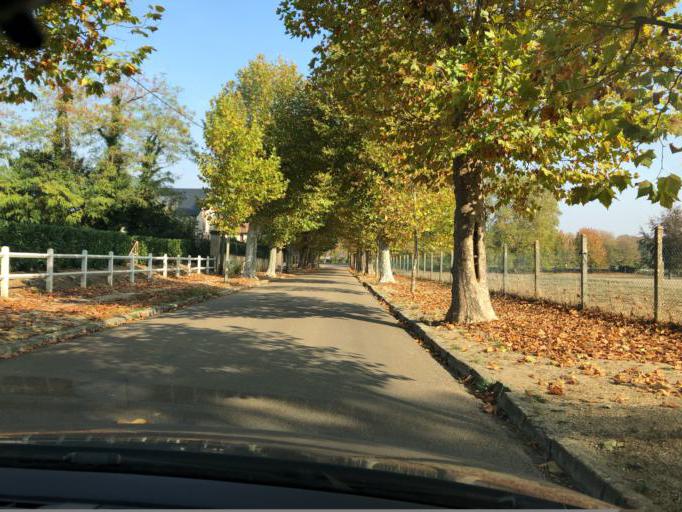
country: FR
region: Bourgogne
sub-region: Departement de l'Yonne
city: Champigny
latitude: 48.3211
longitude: 3.1300
